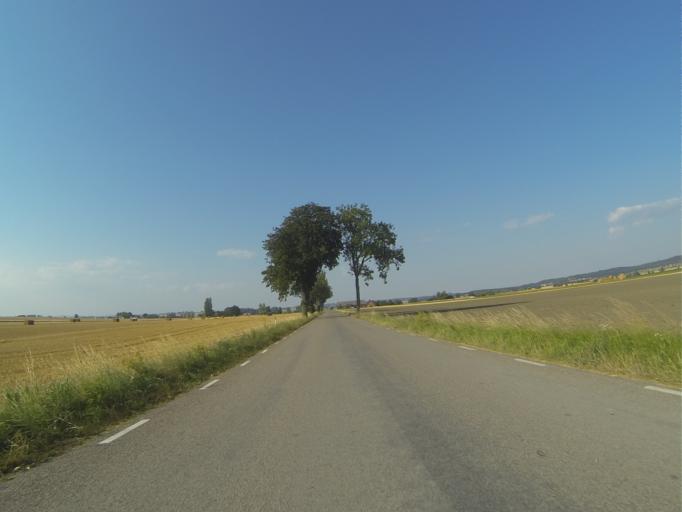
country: SE
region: Skane
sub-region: Lunds Kommun
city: Genarp
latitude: 55.6044
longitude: 13.3661
